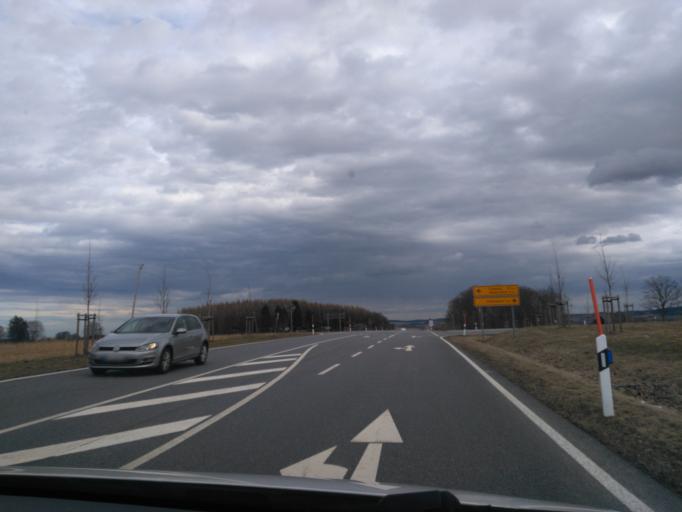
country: DE
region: Saxony
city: Drebach
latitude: 50.6434
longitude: 13.0258
